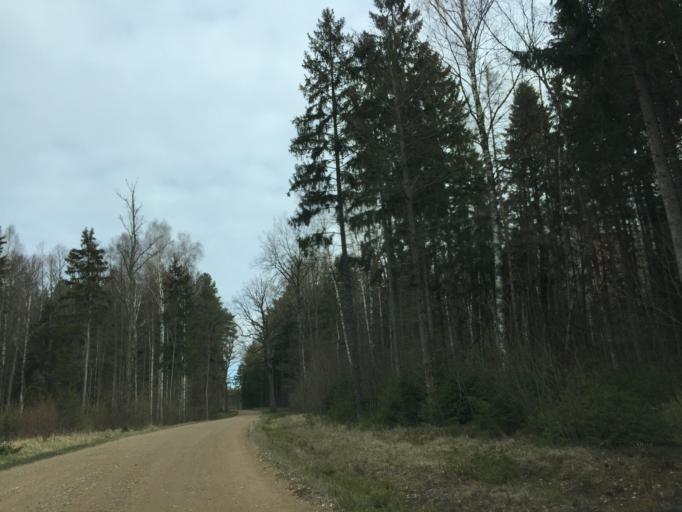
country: LV
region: Saulkrastu
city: Saulkrasti
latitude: 57.5079
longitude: 24.4139
